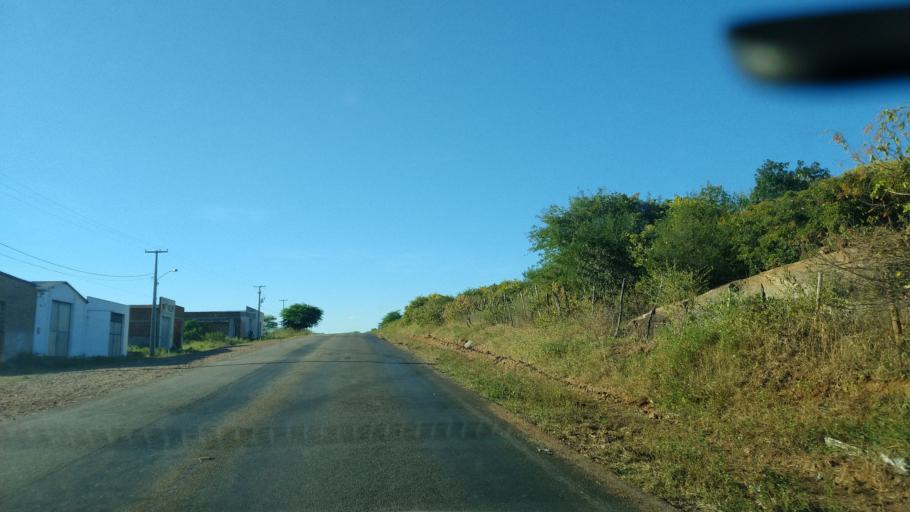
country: BR
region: Rio Grande do Norte
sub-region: Sao Jose Do Campestre
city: Sao Jose do Campestre
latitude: -6.3082
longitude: -35.7155
